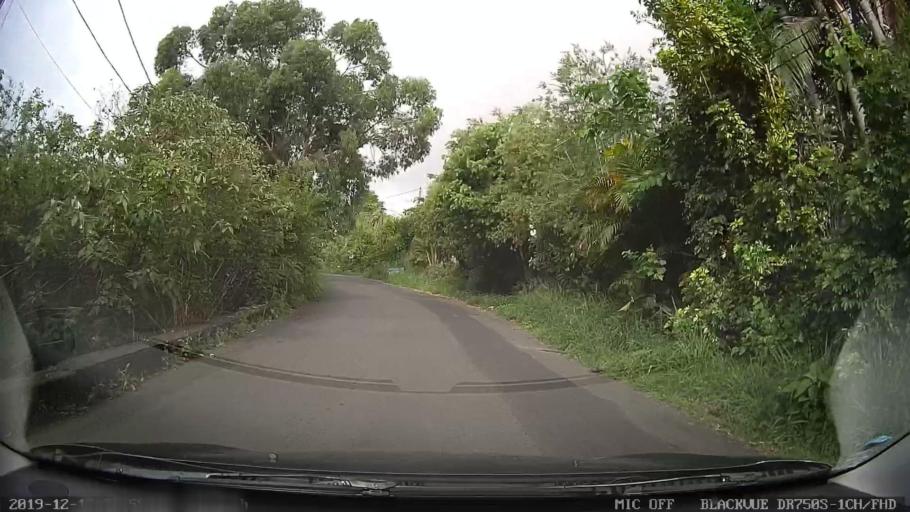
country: RE
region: Reunion
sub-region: Reunion
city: Le Tampon
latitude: -21.2575
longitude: 55.5154
